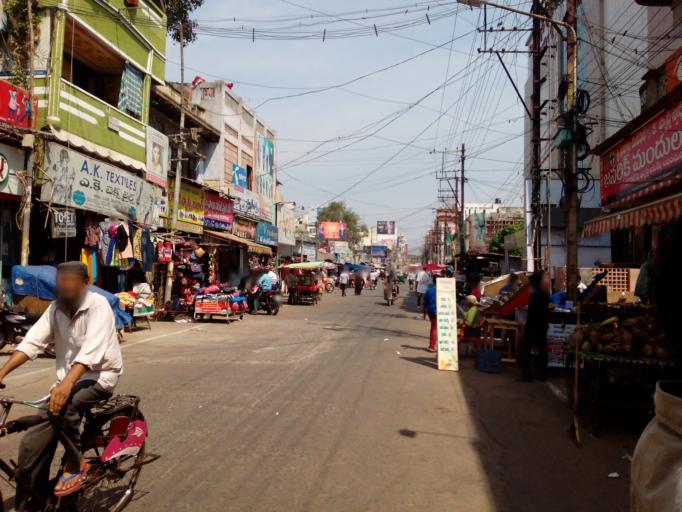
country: IN
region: Andhra Pradesh
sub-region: Krishna
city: Vijayawada
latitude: 16.5090
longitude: 80.6236
